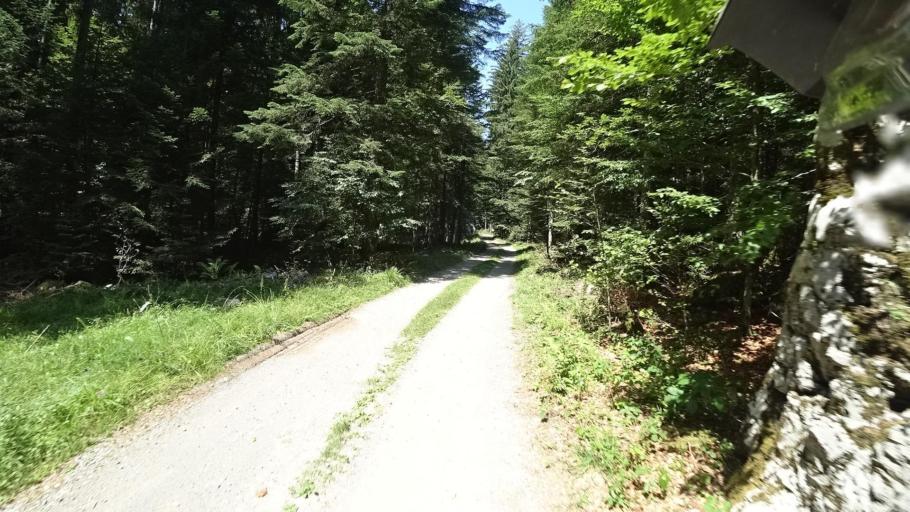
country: HR
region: Primorsko-Goranska
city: Bribir
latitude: 45.2609
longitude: 14.8937
